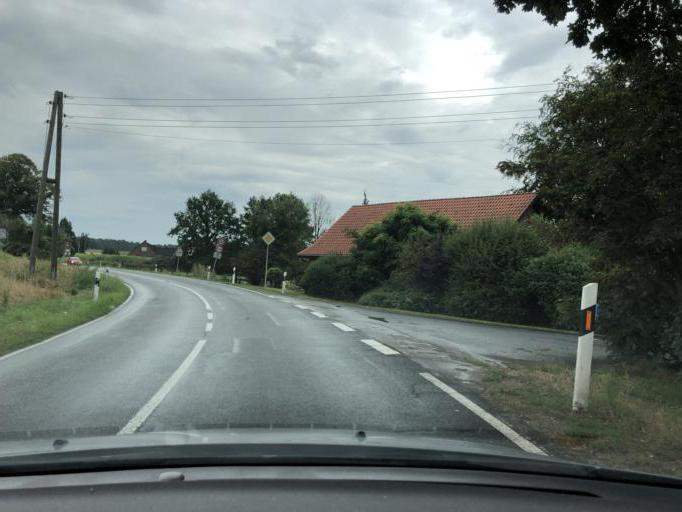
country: DE
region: North Rhine-Westphalia
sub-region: Regierungsbezirk Dusseldorf
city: Schermbeck
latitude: 51.6465
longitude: 6.8940
